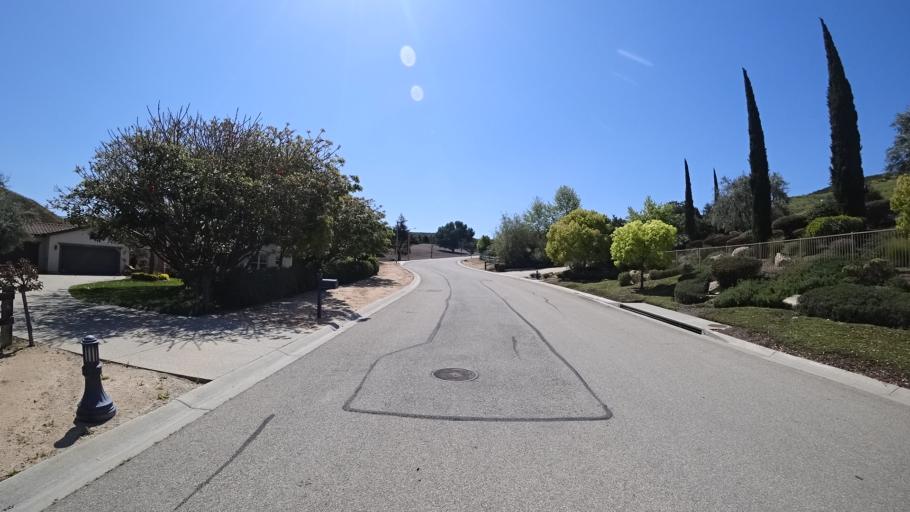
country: US
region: California
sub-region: Ventura County
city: Moorpark
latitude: 34.2475
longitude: -118.8434
